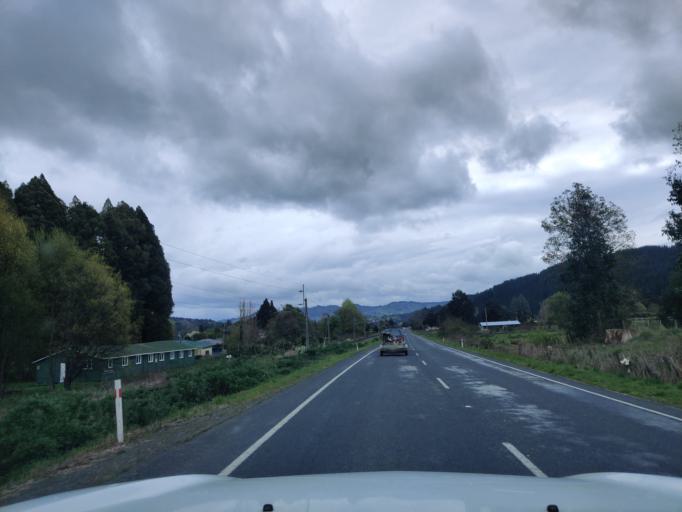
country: NZ
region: Waikato
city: Turangi
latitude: -38.8812
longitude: 175.2973
